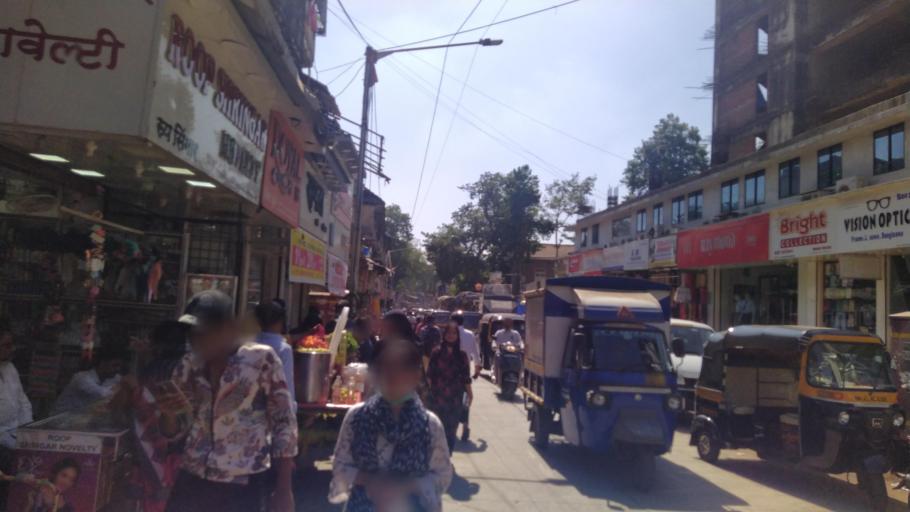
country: IN
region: Maharashtra
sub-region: Mumbai Suburban
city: Mumbai
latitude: 19.0665
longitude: 72.8776
